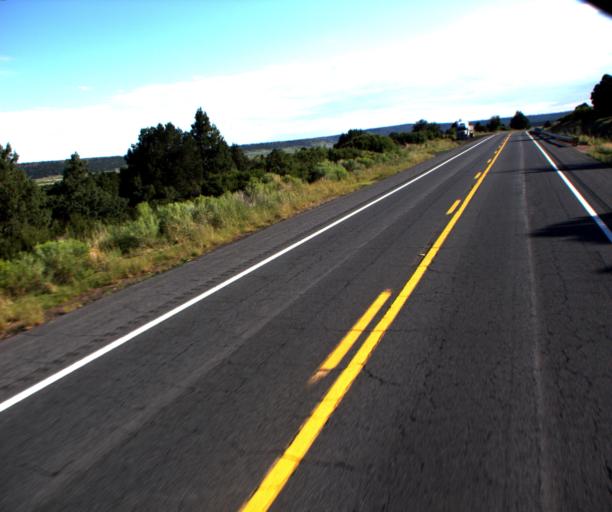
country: US
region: Arizona
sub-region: Apache County
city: Eagar
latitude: 33.9673
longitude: -109.2040
